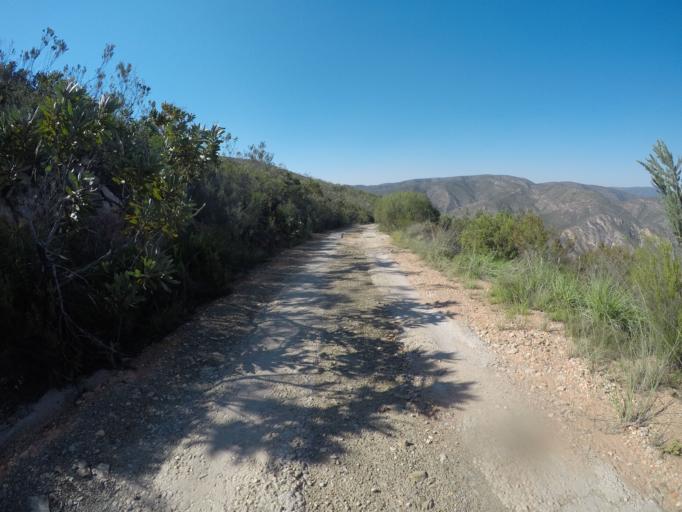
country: ZA
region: Eastern Cape
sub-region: Cacadu District Municipality
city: Kareedouw
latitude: -33.6384
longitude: 24.4510
